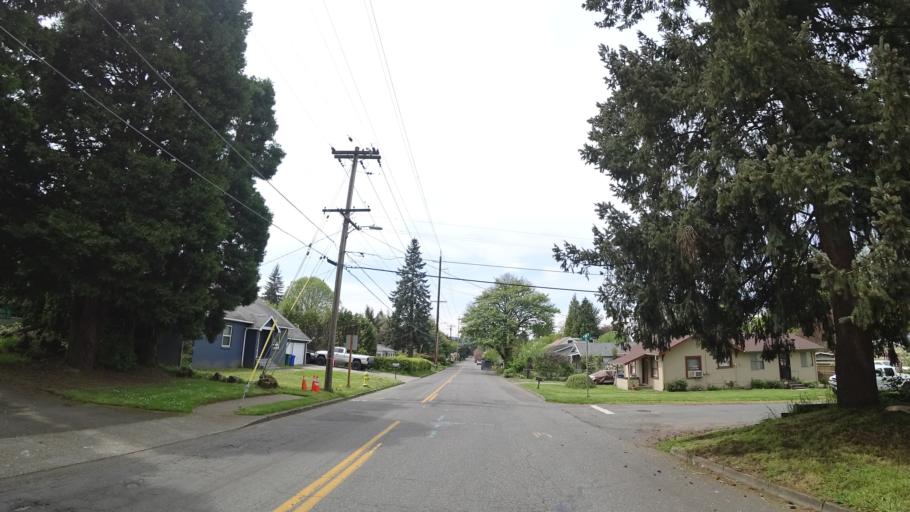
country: US
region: Oregon
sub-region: Clackamas County
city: Milwaukie
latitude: 45.4514
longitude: -122.6234
